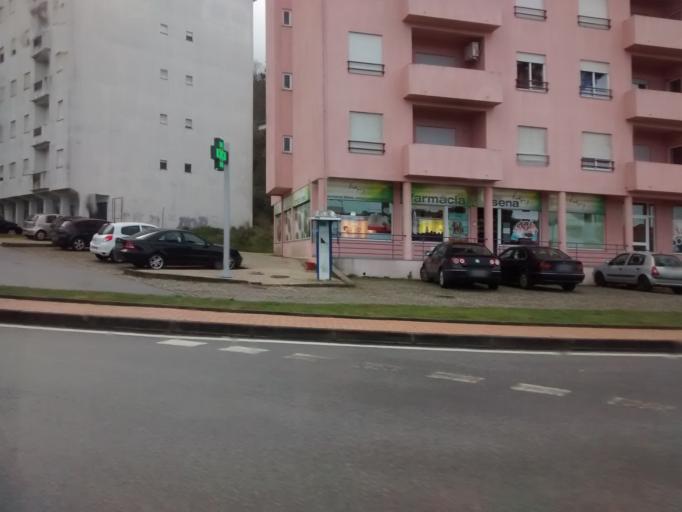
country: PT
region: Guarda
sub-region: Seia
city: Seia
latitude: 40.4094
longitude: -7.7070
